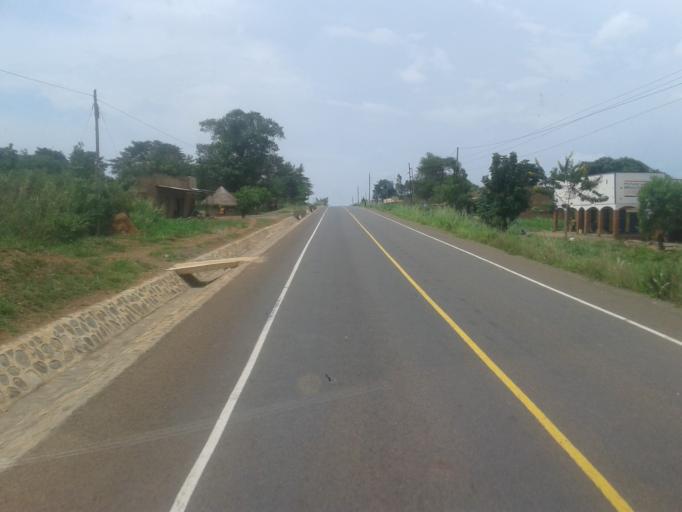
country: UG
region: Western Region
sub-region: Kiryandongo District
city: Kiryandongo
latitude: 1.8837
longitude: 32.0673
